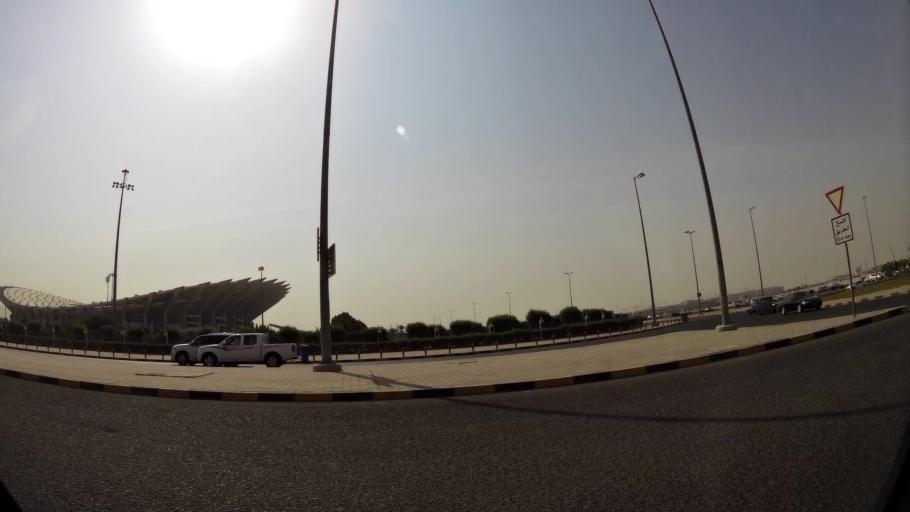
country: KW
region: Al Asimah
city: Ar Rabiyah
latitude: 29.2747
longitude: 47.9163
